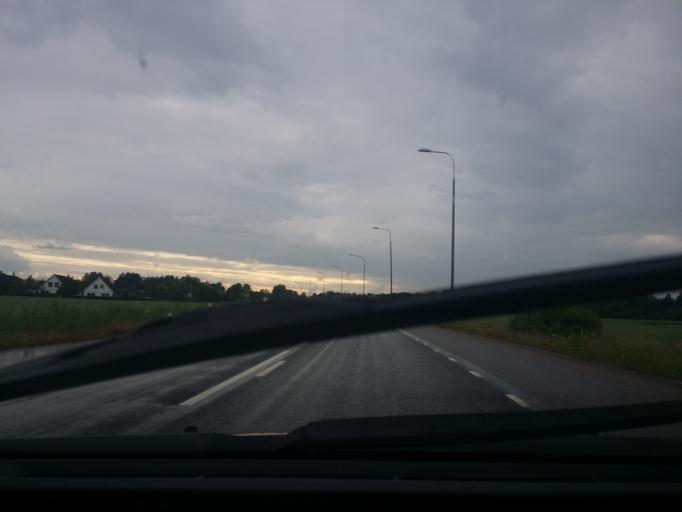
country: SE
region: Vaestmanland
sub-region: Arboga Kommun
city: Arboga
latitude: 59.4055
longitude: 15.8484
